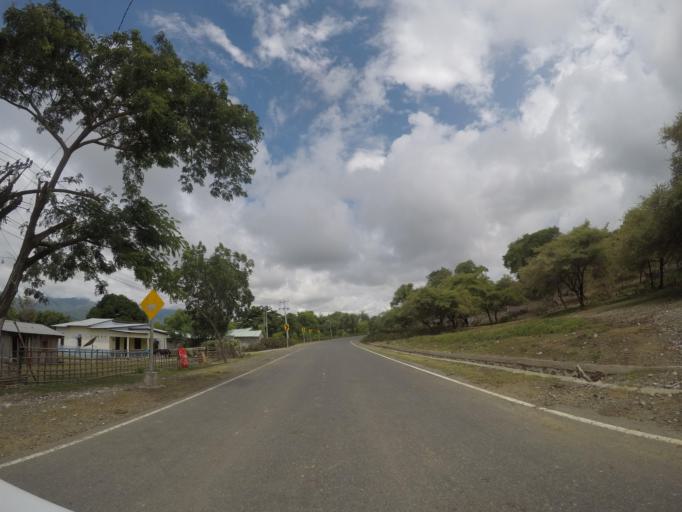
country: TL
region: Liquica
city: Maubara
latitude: -8.7443
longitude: 125.1119
